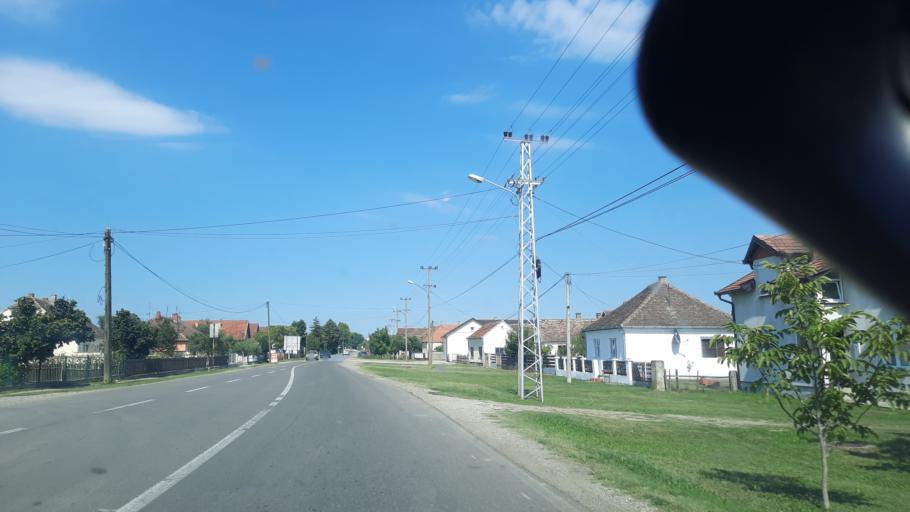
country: RS
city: Macvanska Mitrovica
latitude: 44.9569
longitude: 19.6009
